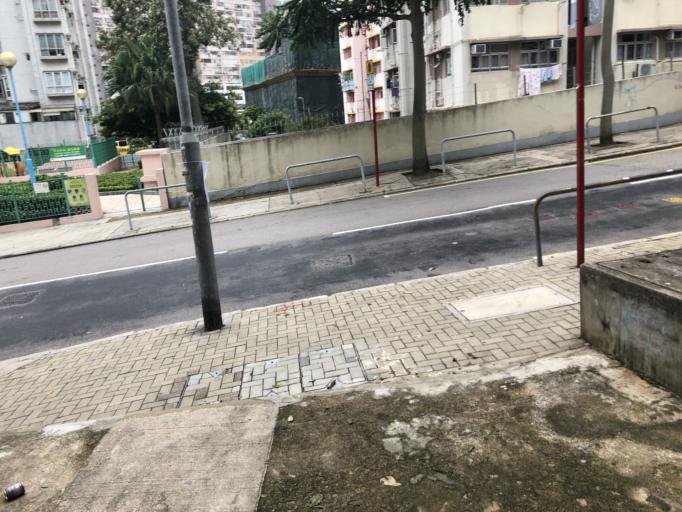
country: HK
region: Wanchai
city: Wan Chai
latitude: 22.2650
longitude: 114.2444
